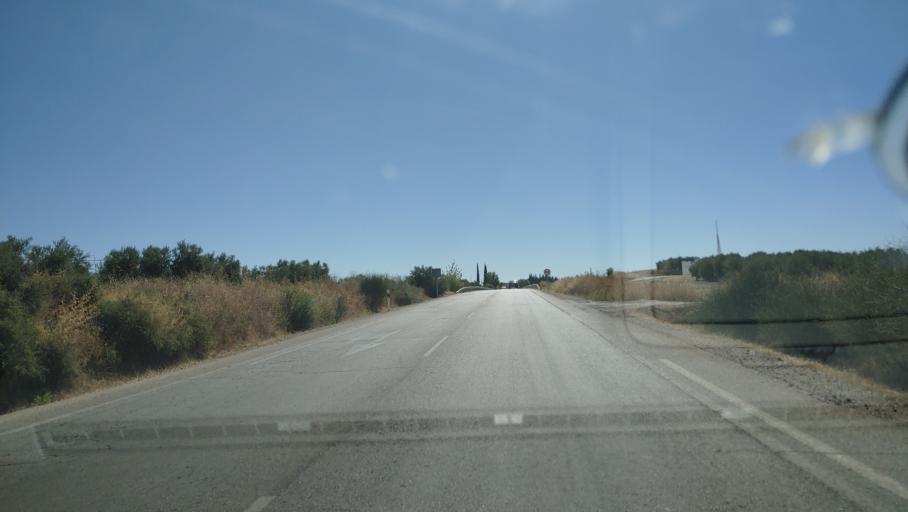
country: ES
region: Andalusia
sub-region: Provincia de Jaen
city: Villacarrillo
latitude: 38.1275
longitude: -3.0606
